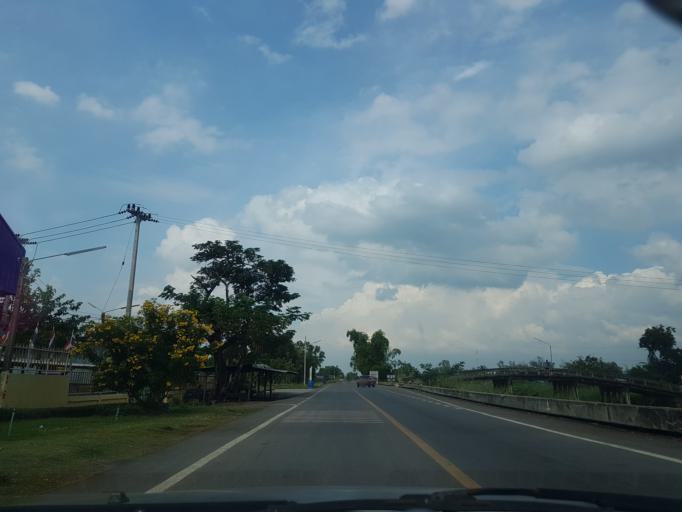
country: TH
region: Pathum Thani
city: Nong Suea
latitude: 14.2199
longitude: 100.8914
